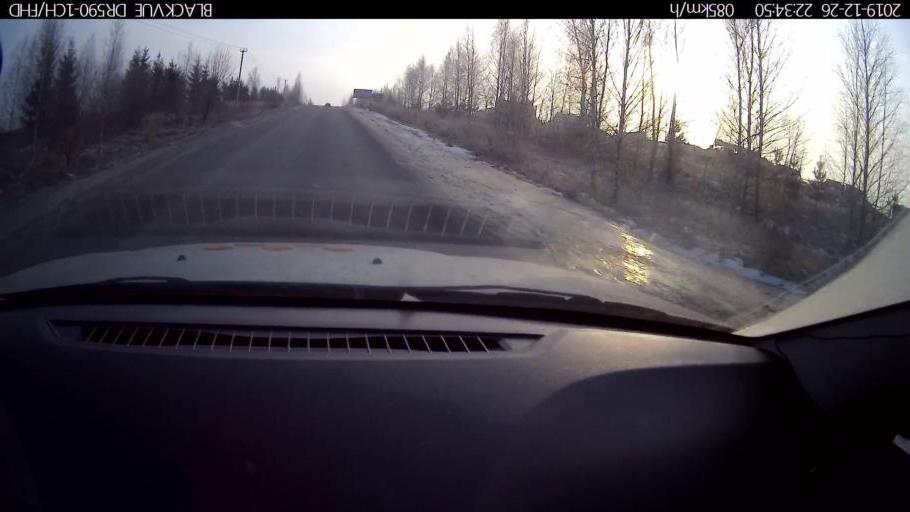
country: RU
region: Nizjnij Novgorod
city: Burevestnik
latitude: 56.1524
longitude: 43.7138
